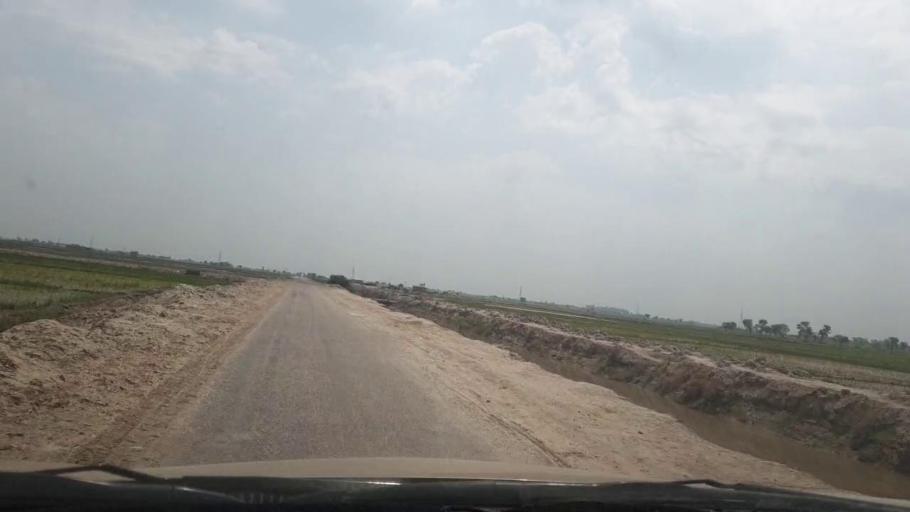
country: PK
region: Sindh
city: Ratodero
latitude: 27.7006
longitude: 68.2417
